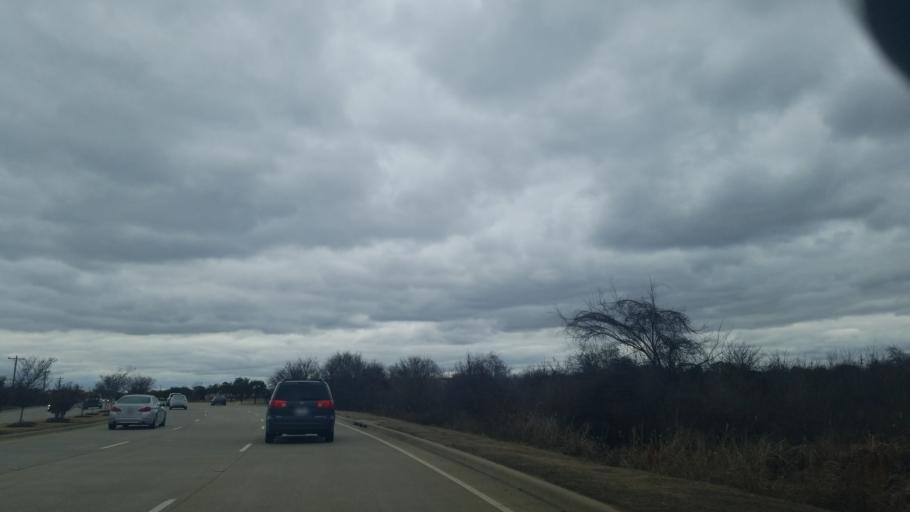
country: US
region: Texas
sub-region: Denton County
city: Double Oak
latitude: 33.0609
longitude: -97.0756
